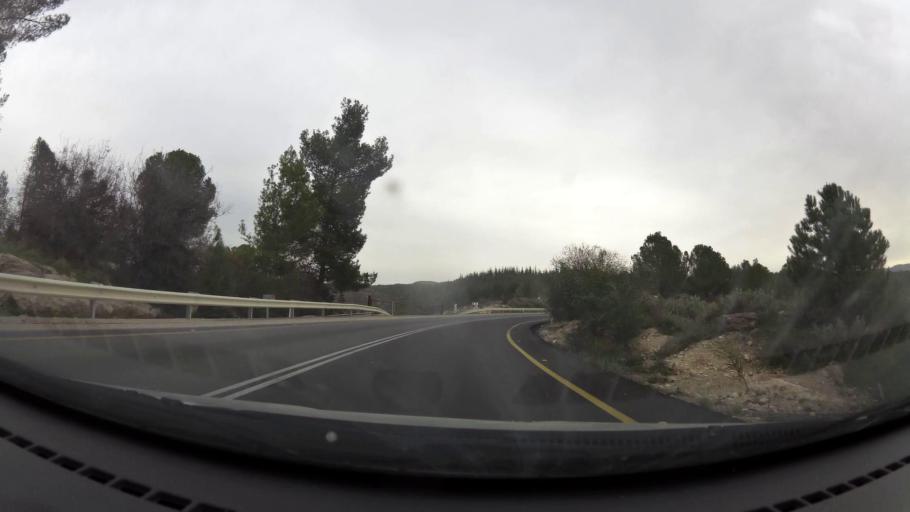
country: PS
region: West Bank
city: Surif
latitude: 31.6746
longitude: 35.0270
